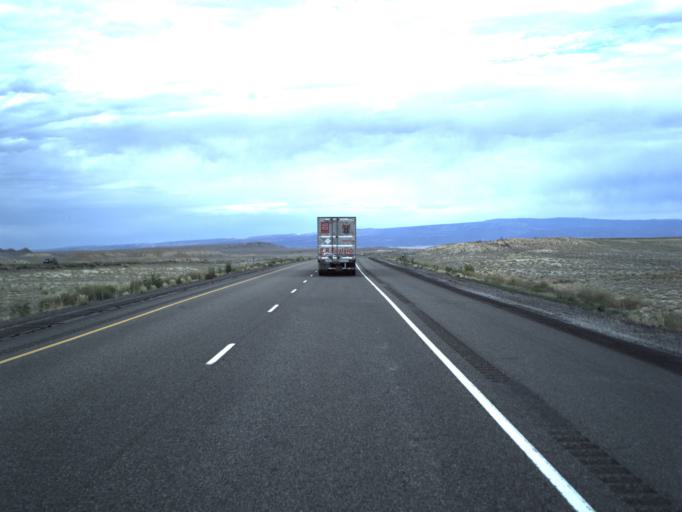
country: US
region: Utah
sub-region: Grand County
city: Moab
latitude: 38.9417
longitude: -109.5441
